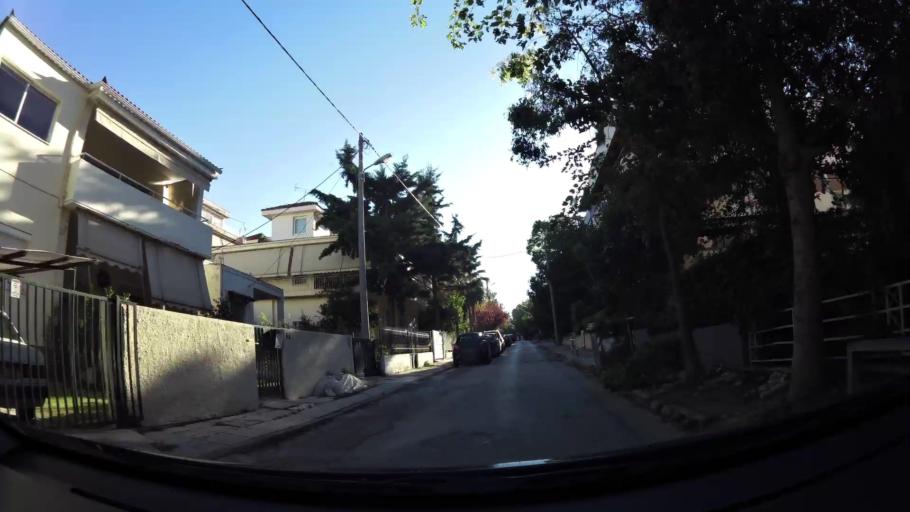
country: GR
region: Attica
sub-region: Nomarchia Athinas
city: Khalandrion
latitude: 38.0158
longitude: 23.7995
